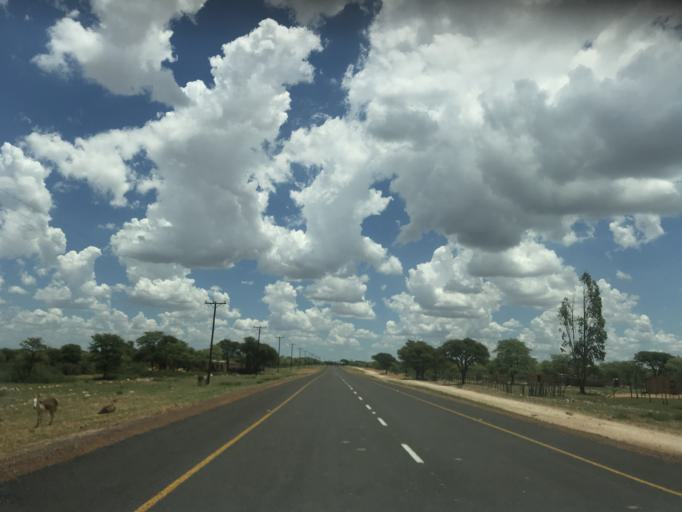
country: BW
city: Mabuli
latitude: -25.8039
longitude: 24.8251
